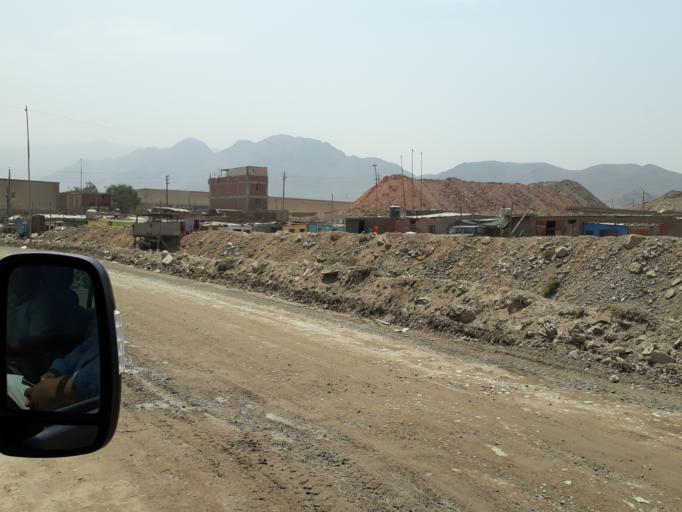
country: PE
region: Lima
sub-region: Lima
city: Santa Maria
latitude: -12.0007
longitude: -76.9168
